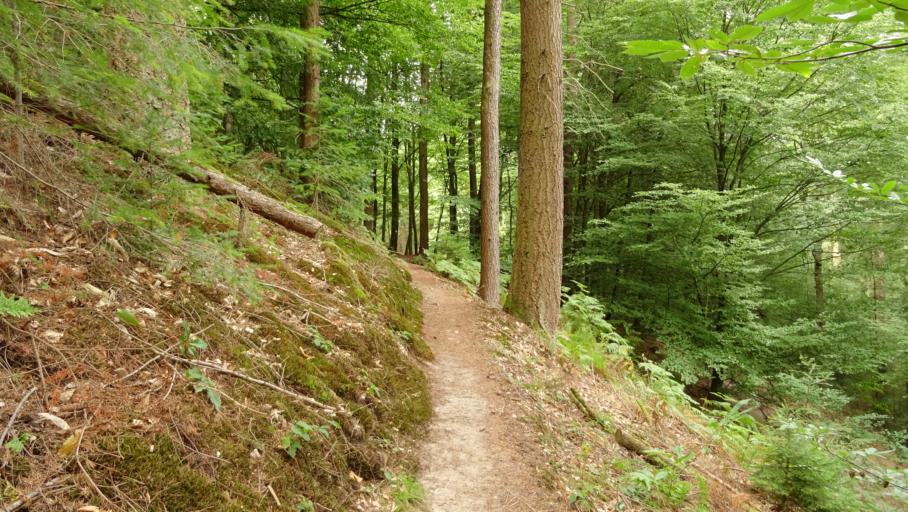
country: DE
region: Baden-Wuerttemberg
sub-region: Karlsruhe Region
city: Neunkirchen
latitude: 49.4222
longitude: 8.9966
